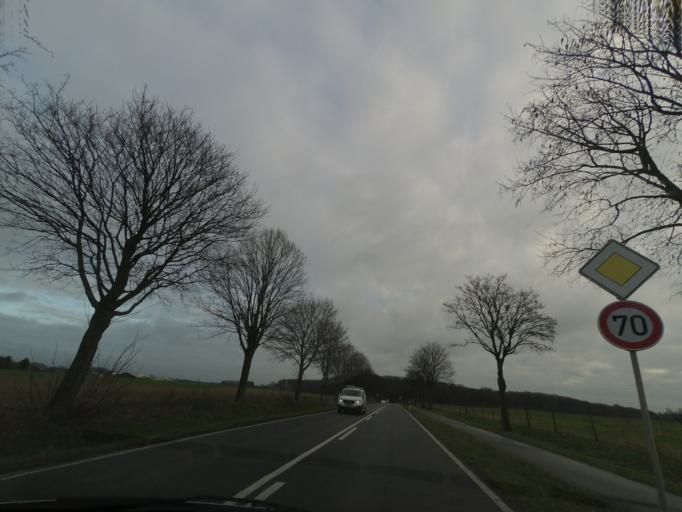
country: DE
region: North Rhine-Westphalia
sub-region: Regierungsbezirk Dusseldorf
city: Juchen
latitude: 51.1399
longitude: 6.5449
